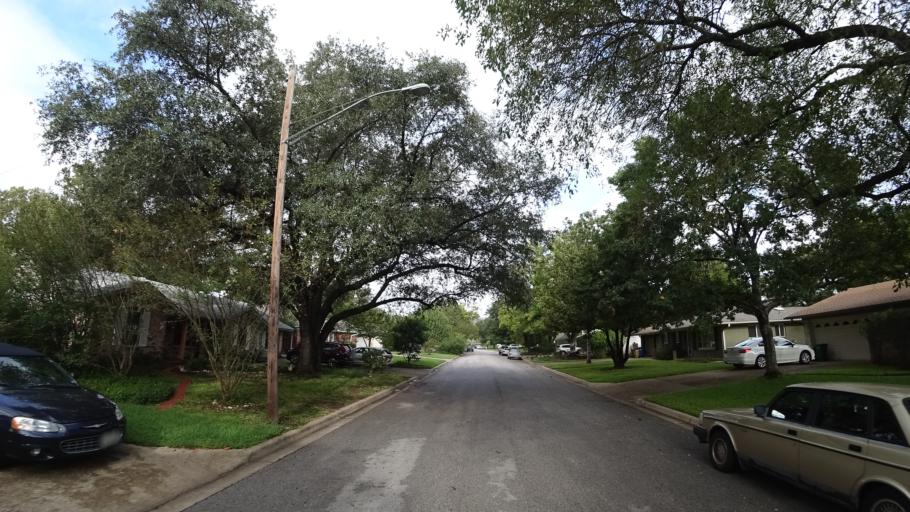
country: US
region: Texas
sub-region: Travis County
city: West Lake Hills
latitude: 30.3574
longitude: -97.7428
